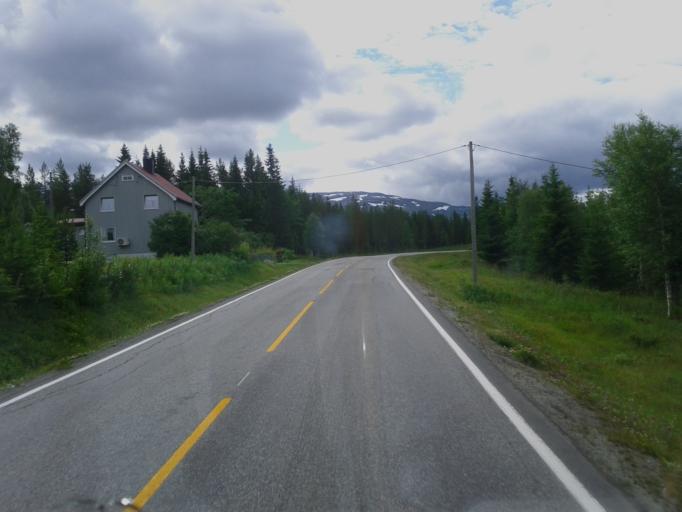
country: NO
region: Nord-Trondelag
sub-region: Hoylandet
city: Hoylandet
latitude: 64.6560
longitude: 12.6495
